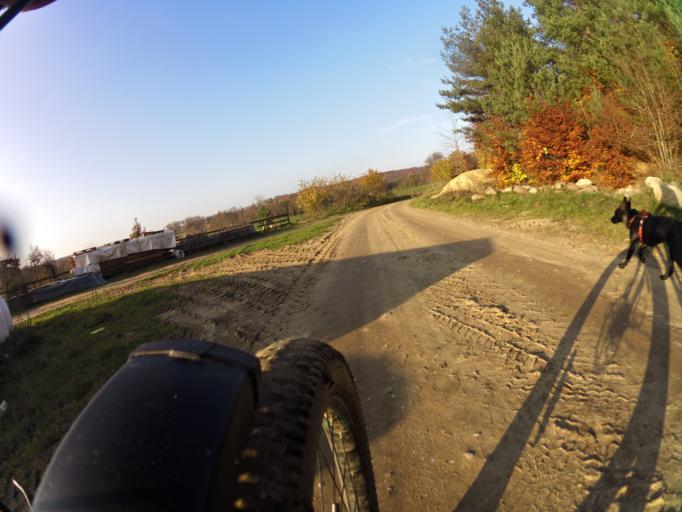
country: PL
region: Pomeranian Voivodeship
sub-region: Powiat pucki
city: Krokowa
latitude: 54.7471
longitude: 18.1954
